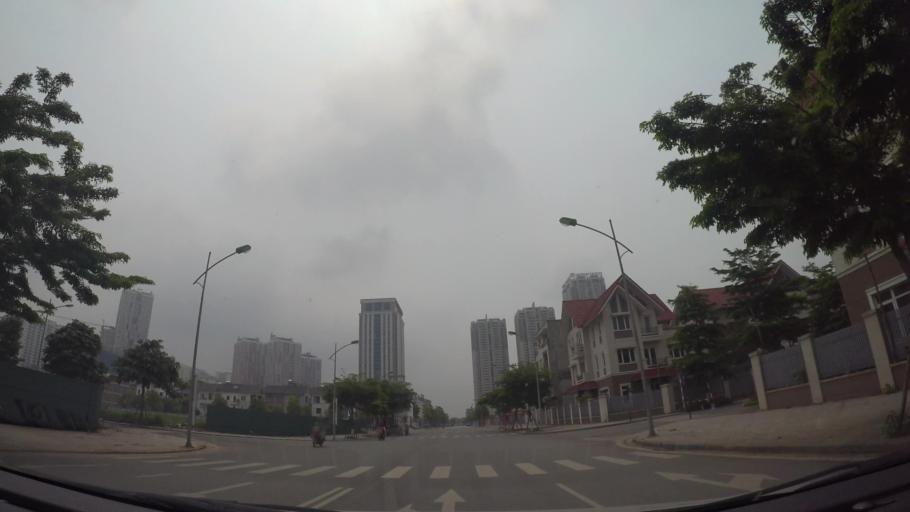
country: VN
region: Ha Noi
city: Ha Dong
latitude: 20.9765
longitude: 105.7558
